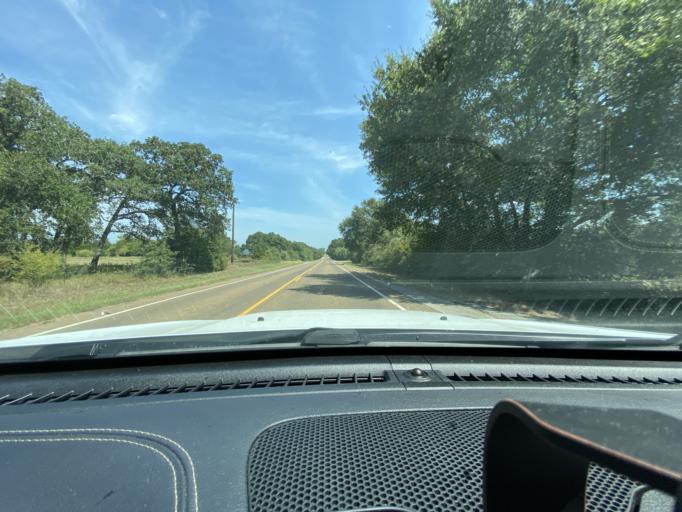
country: US
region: Texas
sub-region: Bastrop County
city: Smithville
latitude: 30.0780
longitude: -97.0885
